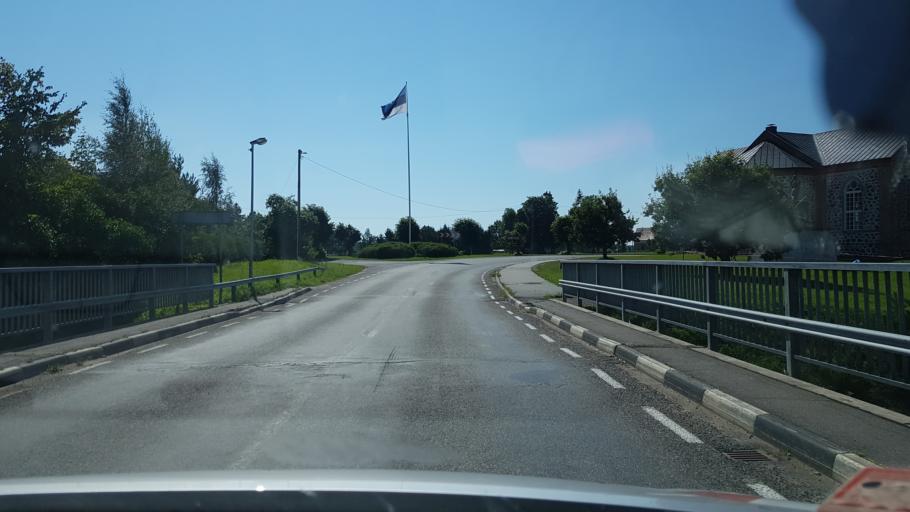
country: EE
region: Paernumaa
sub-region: Tootsi vald
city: Tootsi
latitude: 58.4838
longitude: 24.8148
